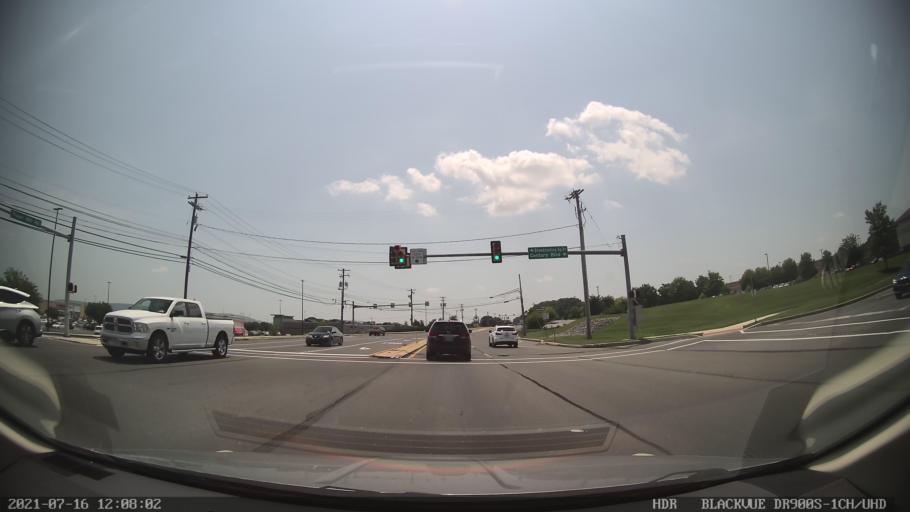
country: US
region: Pennsylvania
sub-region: Berks County
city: Spring Ridge
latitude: 40.3587
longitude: -75.9858
